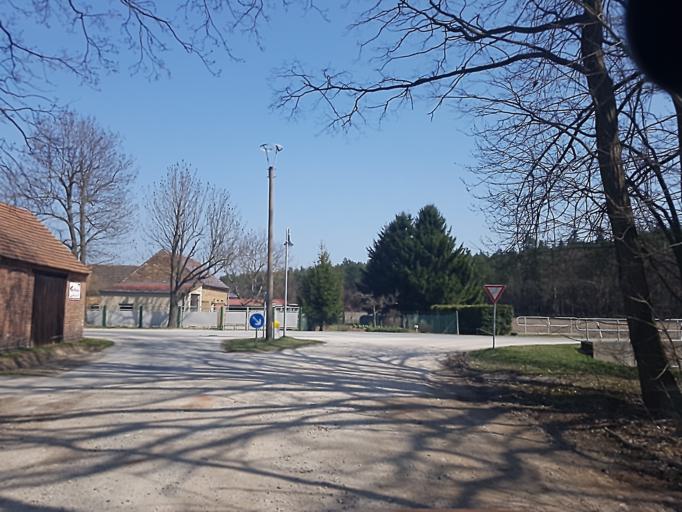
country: DE
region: Brandenburg
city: Forst
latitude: 51.6752
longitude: 14.5730
